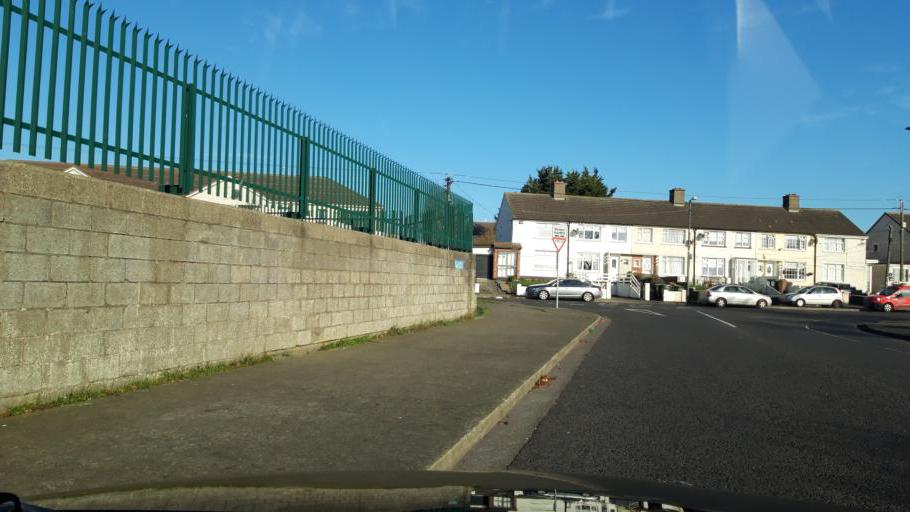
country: IE
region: Leinster
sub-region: Dublin City
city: Finglas
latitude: 53.3839
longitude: -6.3161
